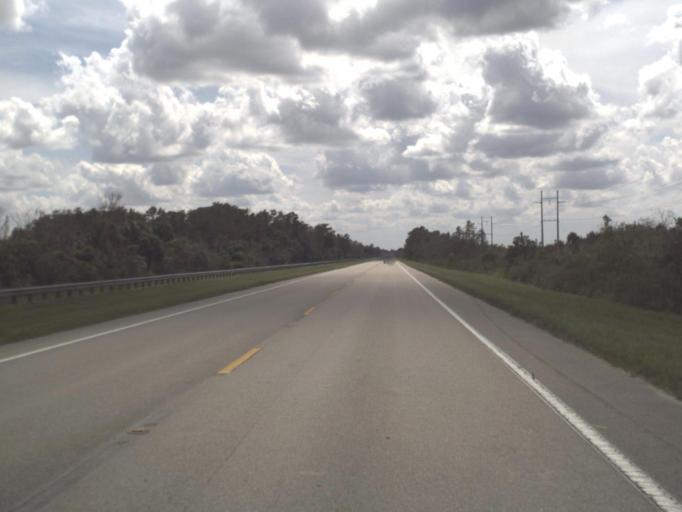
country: US
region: Florida
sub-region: Collier County
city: Orangetree
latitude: 26.0777
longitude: -81.3447
